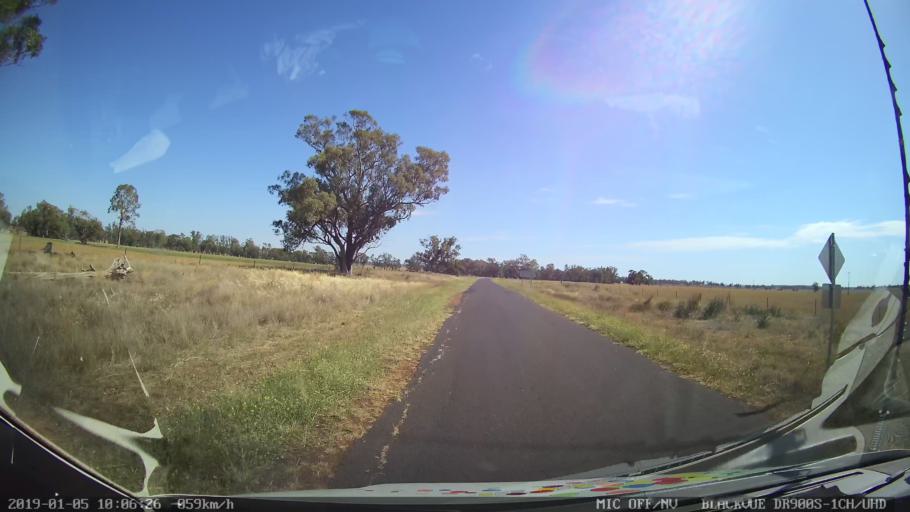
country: AU
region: New South Wales
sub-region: Gilgandra
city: Gilgandra
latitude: -31.6580
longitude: 148.8697
